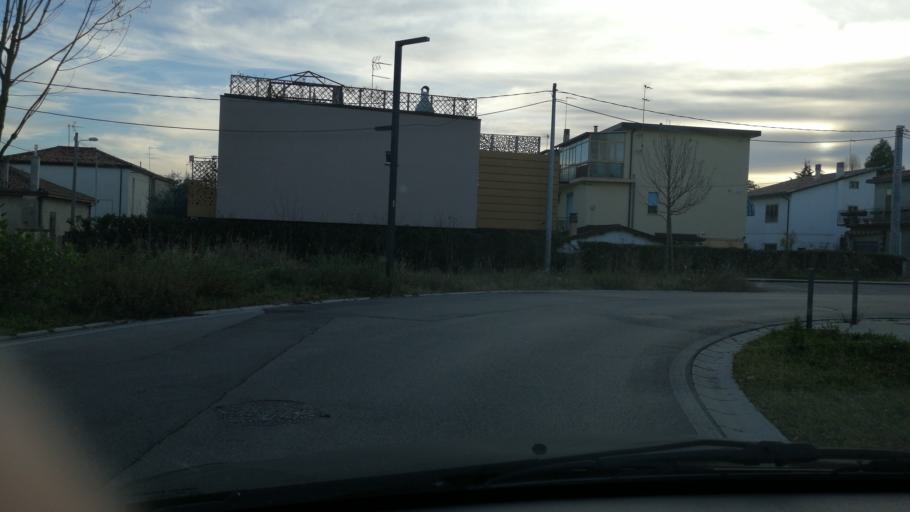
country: IT
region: Veneto
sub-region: Provincia di Venezia
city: Zelarino
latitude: 45.4882
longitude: 12.2152
